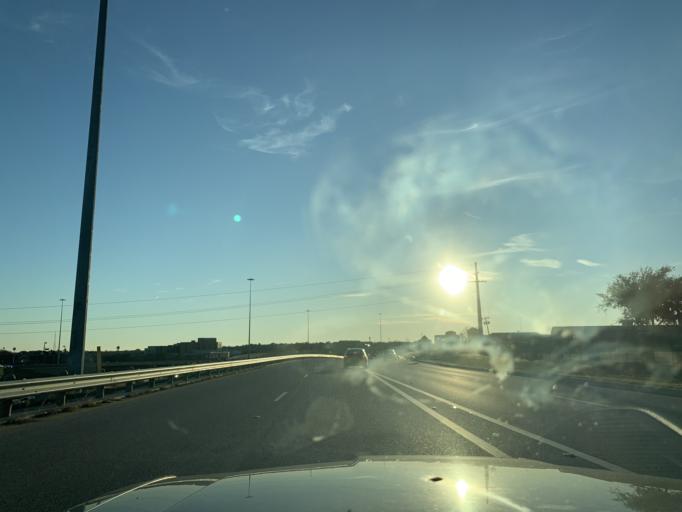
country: US
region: Texas
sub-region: Tarrant County
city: Bedford
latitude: 32.8414
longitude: -97.1191
